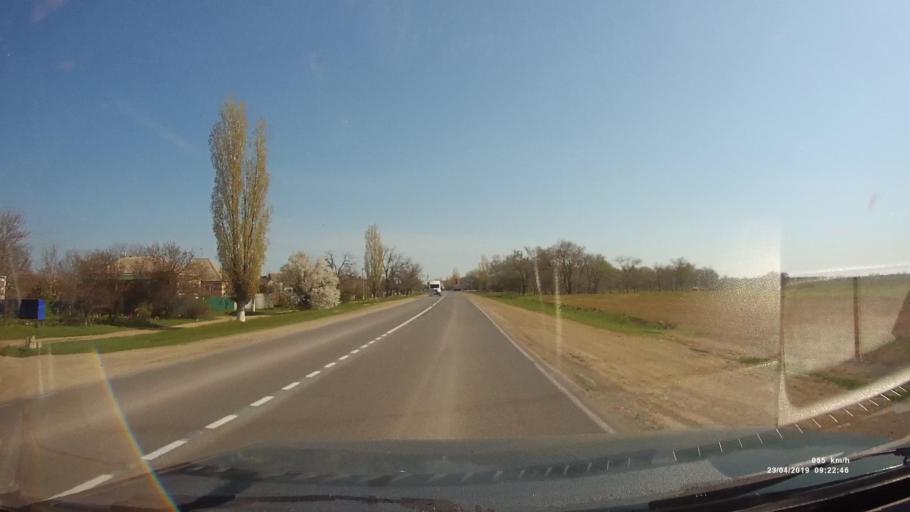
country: RU
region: Rostov
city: Proletarsk
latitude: 46.6927
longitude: 41.7397
